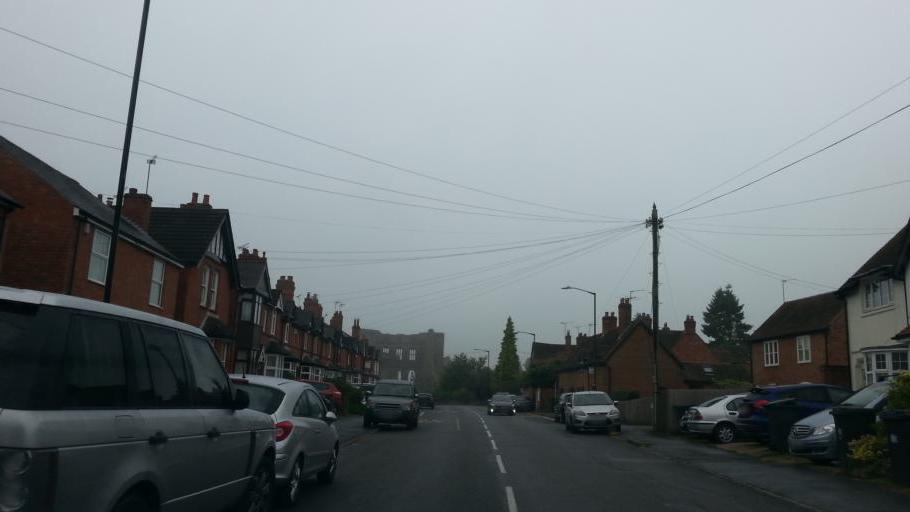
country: GB
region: England
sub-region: Warwickshire
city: Kenilworth
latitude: 52.3503
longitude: -1.5924
